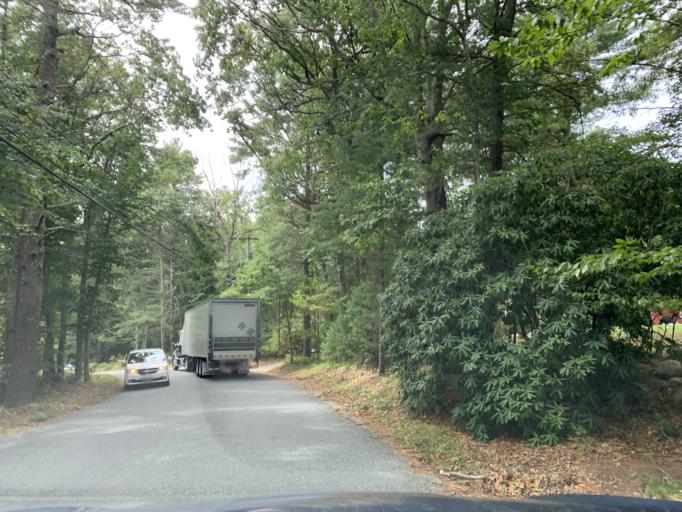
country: US
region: Rhode Island
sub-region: Kent County
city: West Greenwich
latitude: 41.5744
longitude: -71.6225
